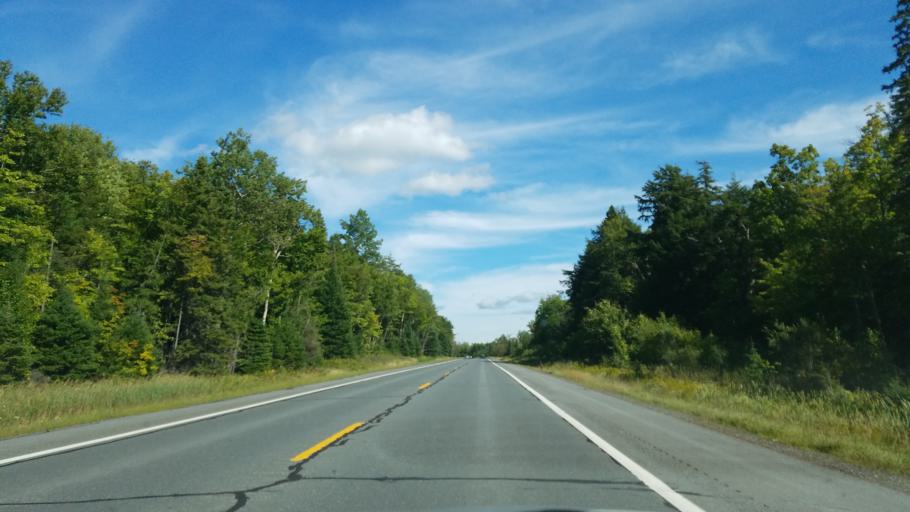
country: US
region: Michigan
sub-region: Baraga County
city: L'Anse
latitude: 46.5803
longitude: -88.4583
